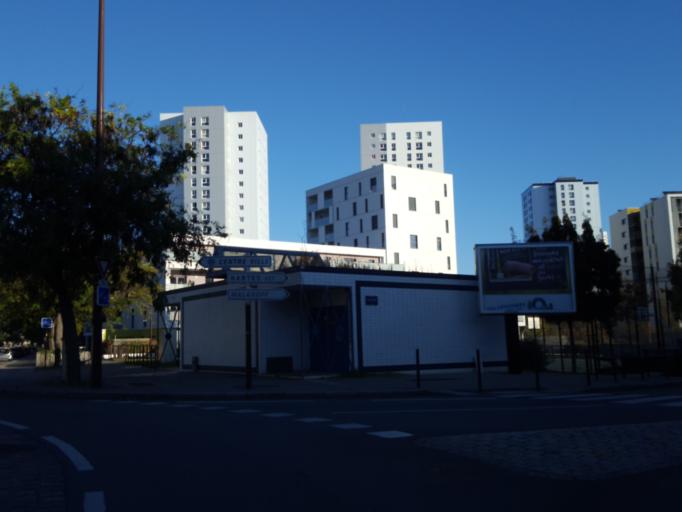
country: FR
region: Pays de la Loire
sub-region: Departement de la Loire-Atlantique
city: Nantes
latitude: 47.2086
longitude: -1.5306
